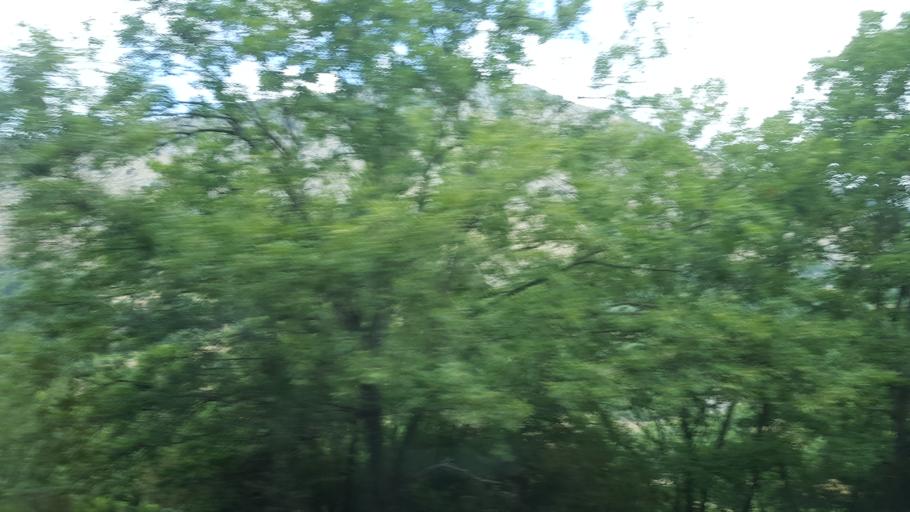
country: AL
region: Vlore
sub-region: Rrethi i Sarandes
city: Dhiver
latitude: 39.9125
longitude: 20.1906
